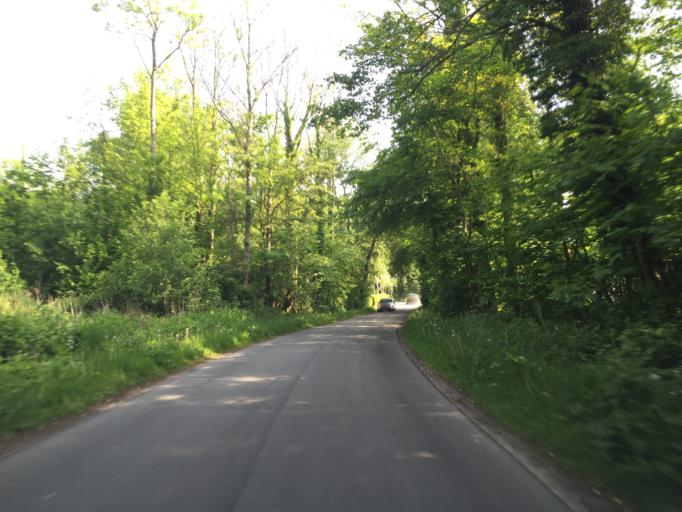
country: DK
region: South Denmark
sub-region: Svendborg Kommune
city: Thuro By
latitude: 55.1330
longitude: 10.7785
